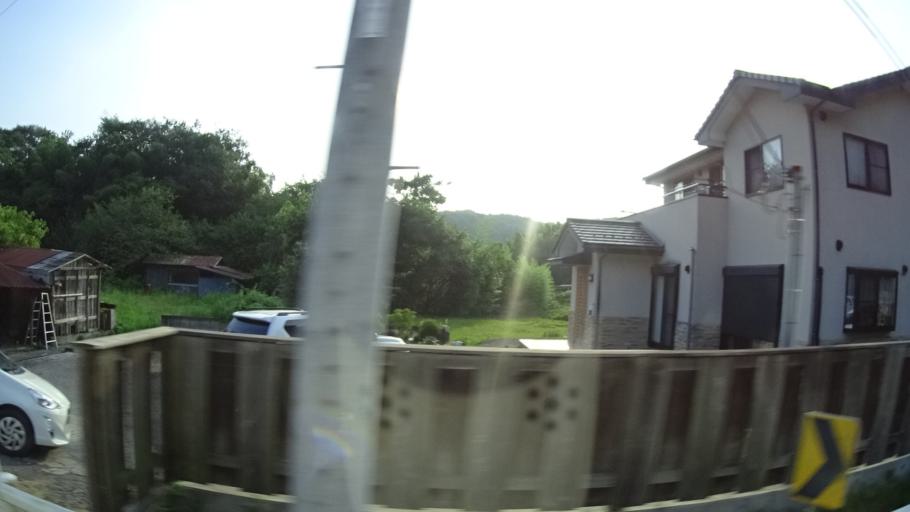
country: JP
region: Tochigi
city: Karasuyama
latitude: 36.6306
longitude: 140.1526
